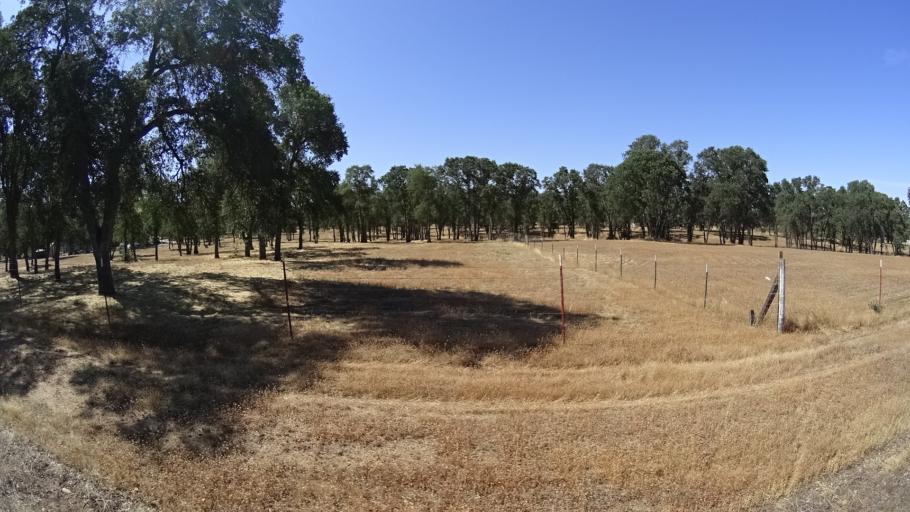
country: US
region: California
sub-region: Calaveras County
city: Rancho Calaveras
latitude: 38.1339
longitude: -120.9198
